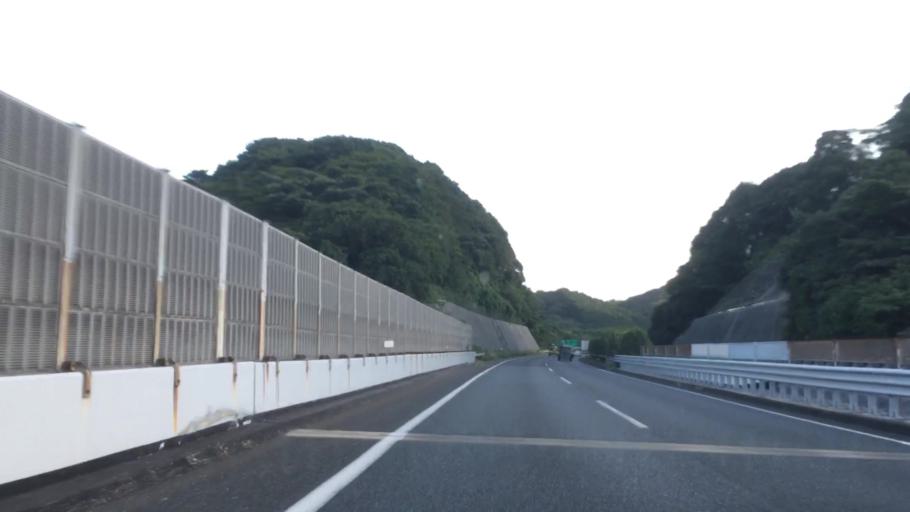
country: JP
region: Yamaguchi
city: Shimonoseki
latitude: 33.8984
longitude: 130.9721
